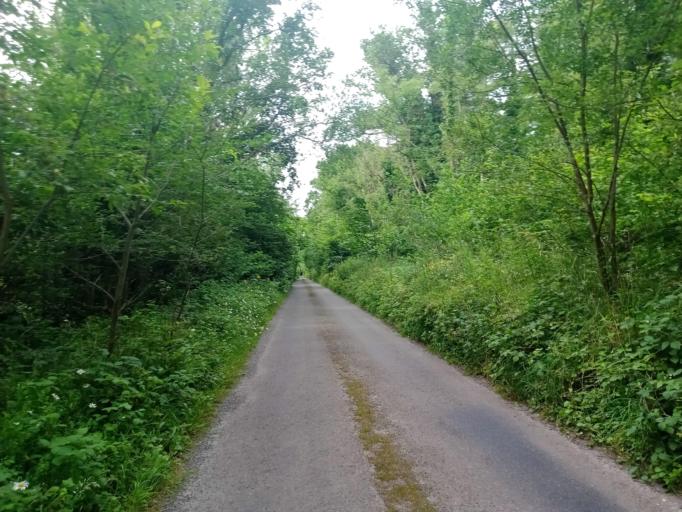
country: IE
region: Leinster
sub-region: Laois
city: Abbeyleix
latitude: 52.9048
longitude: -7.3614
